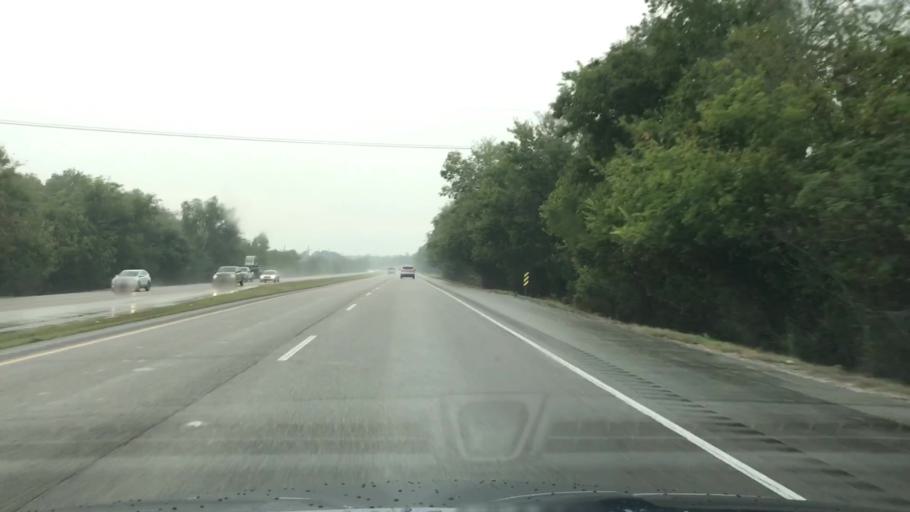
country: US
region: Louisiana
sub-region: Saint Charles Parish
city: Paradis
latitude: 29.8627
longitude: -90.4460
